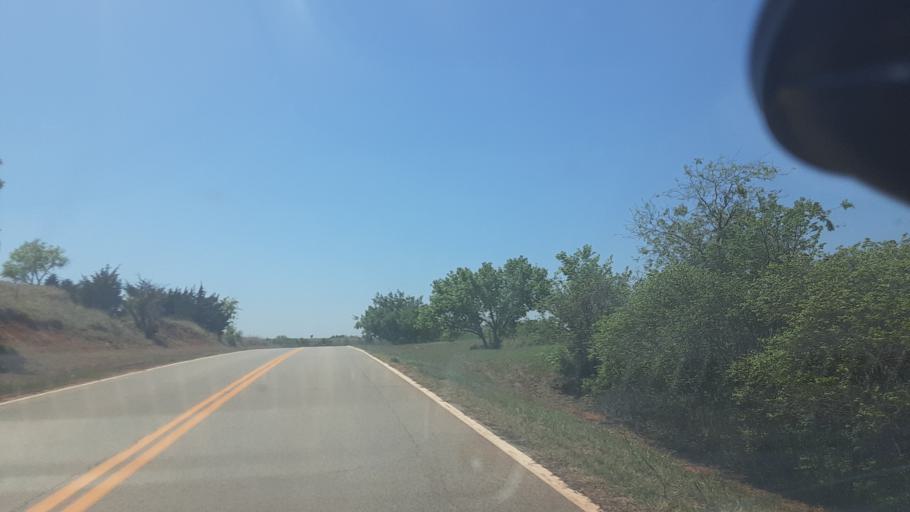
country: US
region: Oklahoma
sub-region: Logan County
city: Langston
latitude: 36.0836
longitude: -97.3984
